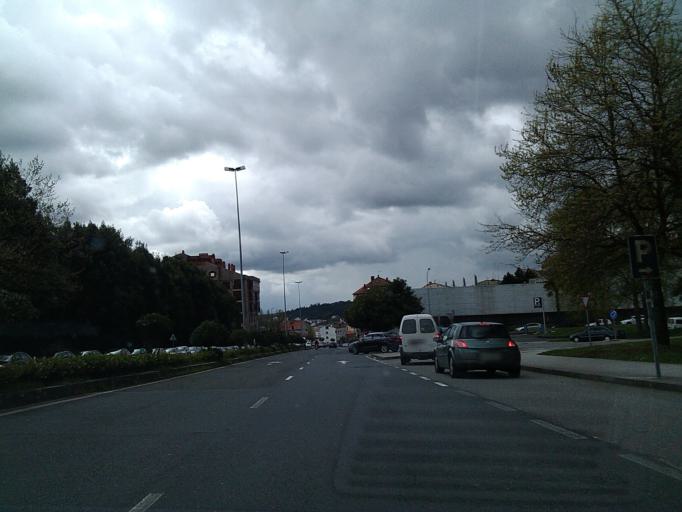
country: ES
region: Galicia
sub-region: Provincia da Coruna
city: Santiago de Compostela
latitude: 42.8887
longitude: -8.5325
